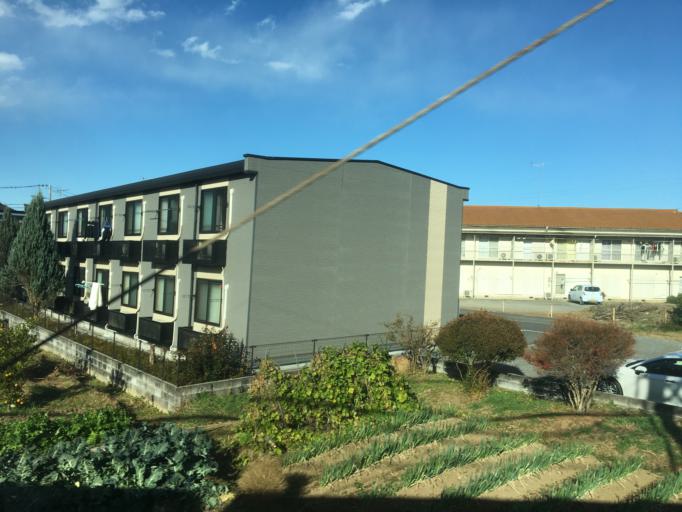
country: JP
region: Saitama
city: Kumagaya
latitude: 36.0466
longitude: 139.3693
